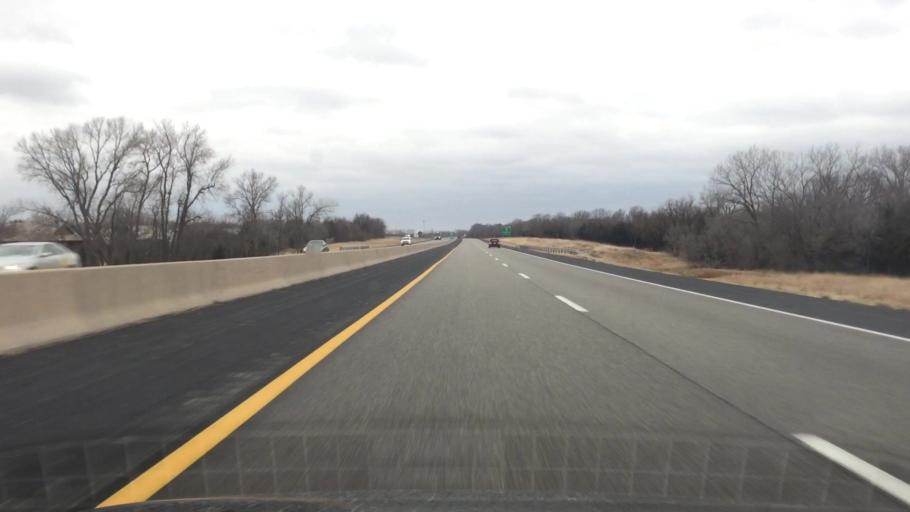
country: US
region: Kansas
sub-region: Butler County
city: Andover
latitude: 37.7000
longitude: -97.1573
